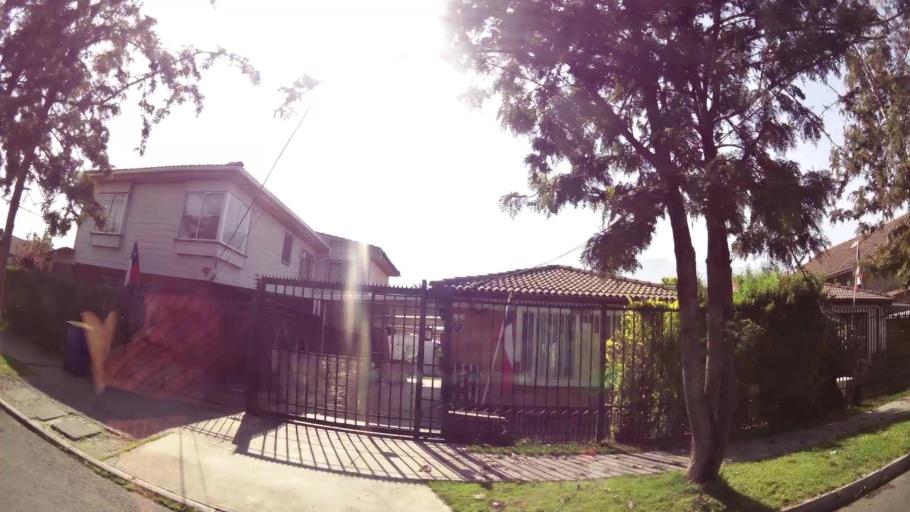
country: CL
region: Santiago Metropolitan
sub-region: Provincia de Santiago
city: Villa Presidente Frei, Nunoa, Santiago, Chile
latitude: -33.5293
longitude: -70.5660
